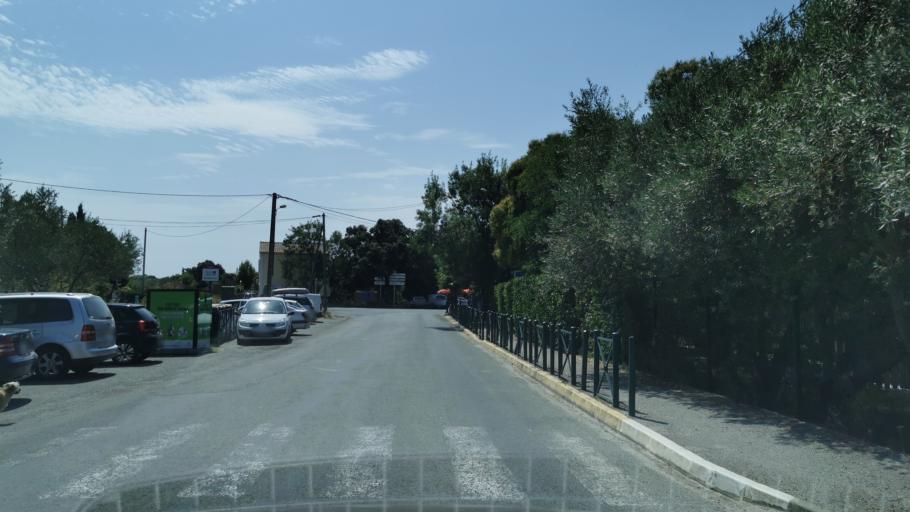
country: FR
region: Languedoc-Roussillon
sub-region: Departement de l'Aude
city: Bize-Minervois
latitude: 43.2997
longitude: 2.8710
